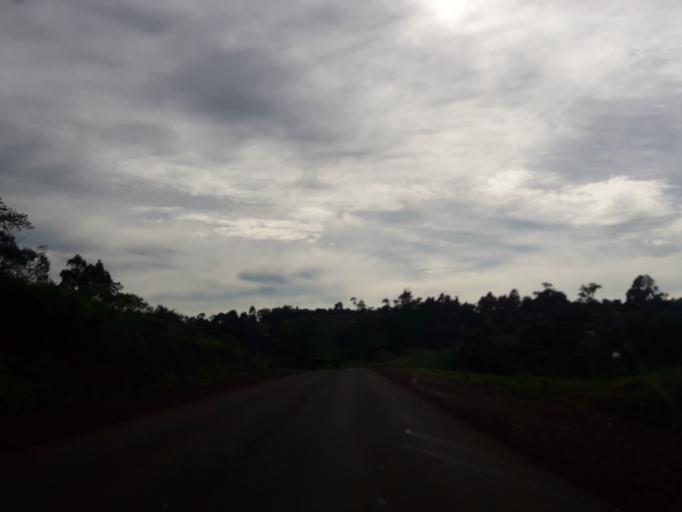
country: AR
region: Misiones
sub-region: Departamento de San Pedro
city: San Pedro
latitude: -26.5125
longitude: -53.9291
